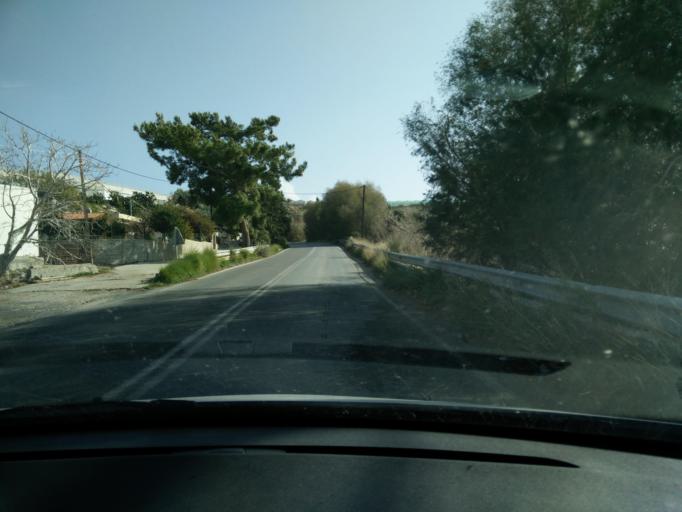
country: GR
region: Crete
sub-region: Nomos Lasithiou
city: Gra Liyia
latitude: 35.0087
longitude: 25.6332
